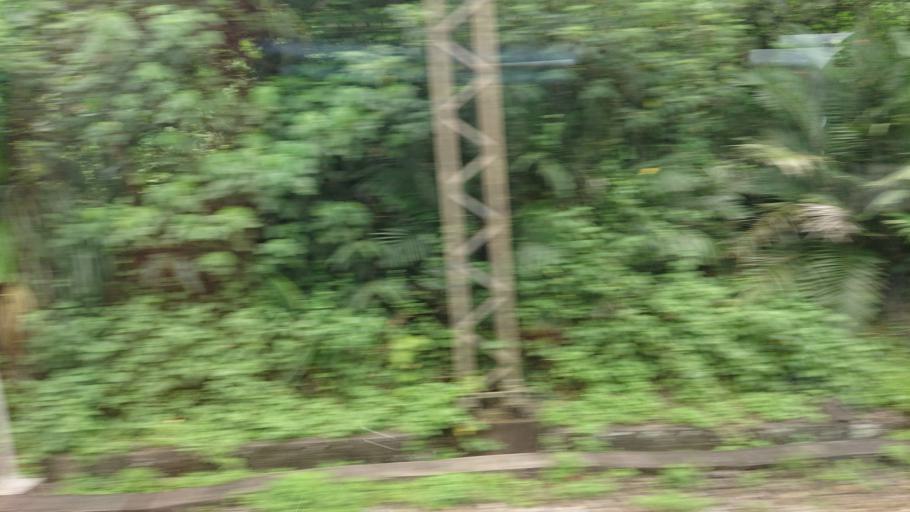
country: TW
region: Taiwan
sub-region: Yilan
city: Yilan
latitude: 24.9068
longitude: 121.8715
